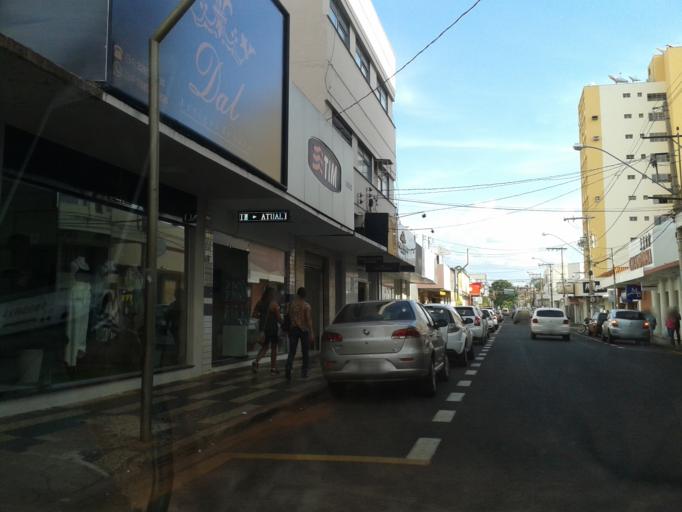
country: BR
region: Minas Gerais
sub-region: Ituiutaba
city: Ituiutaba
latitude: -18.9735
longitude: -49.4638
